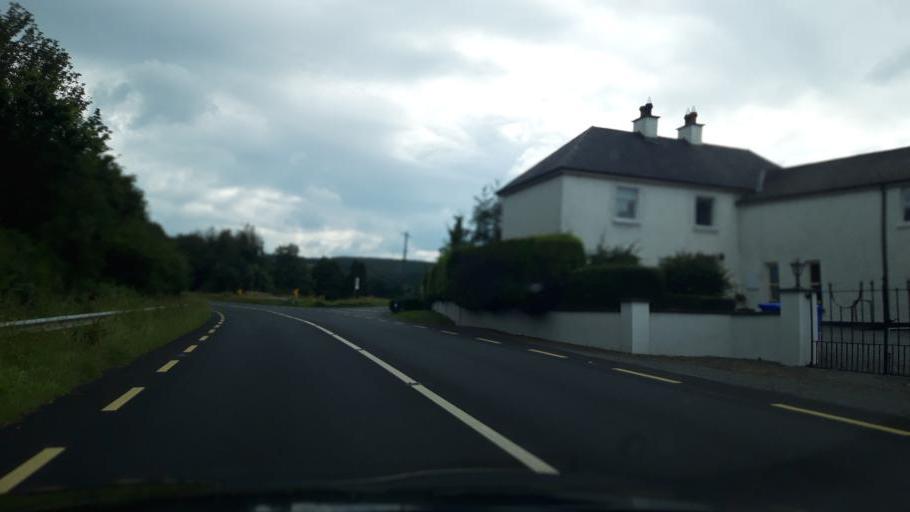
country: IE
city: Ballylinan
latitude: 52.9085
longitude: -7.0875
